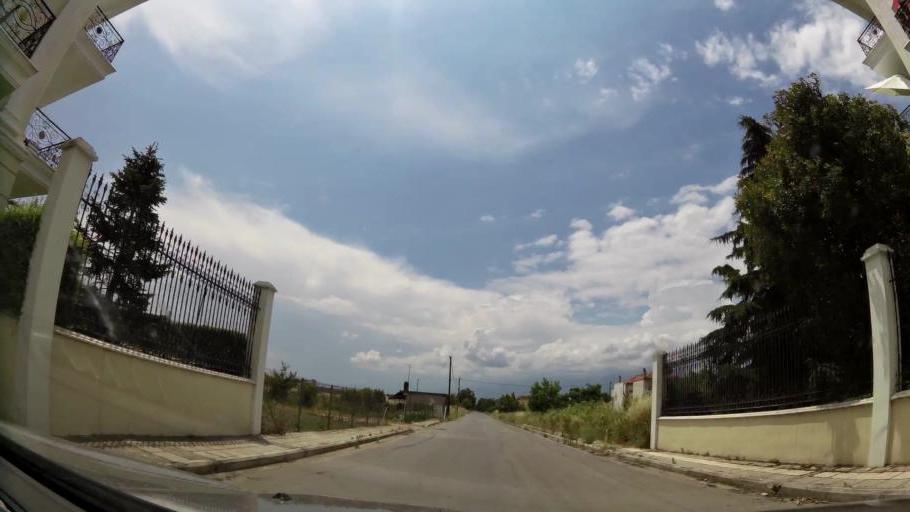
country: GR
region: Central Macedonia
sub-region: Nomos Pierias
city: Katerini
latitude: 40.2659
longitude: 22.5239
